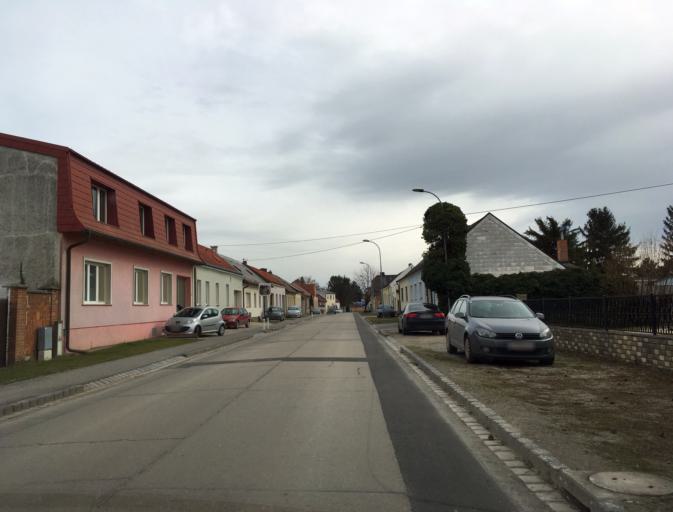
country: AT
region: Lower Austria
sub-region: Politischer Bezirk Ganserndorf
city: Leopoldsdorf im Marchfelde
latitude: 48.2254
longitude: 16.6856
